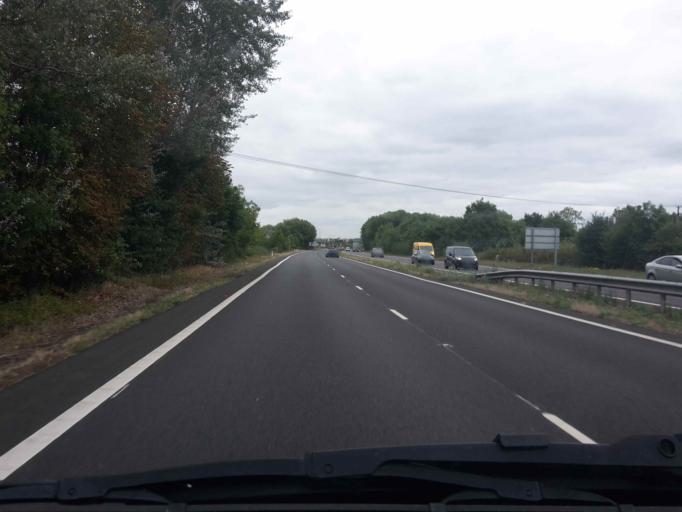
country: GB
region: England
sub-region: Wokingham
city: Swallowfield
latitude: 51.3991
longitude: -0.9845
